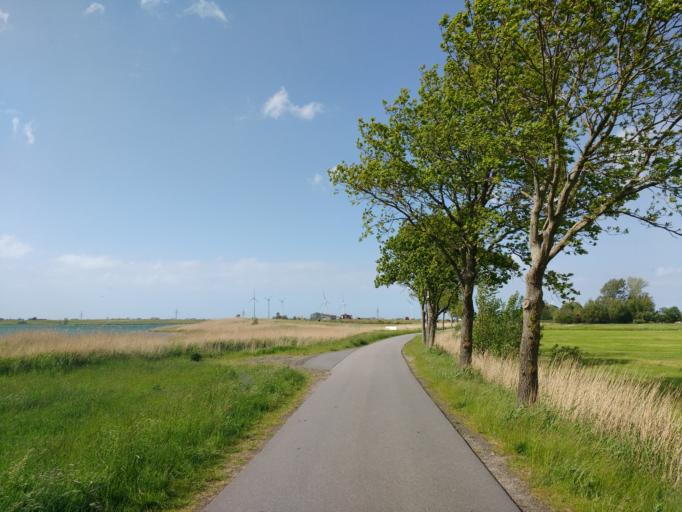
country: DE
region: Lower Saxony
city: Schillig
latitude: 53.6679
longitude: 7.9292
